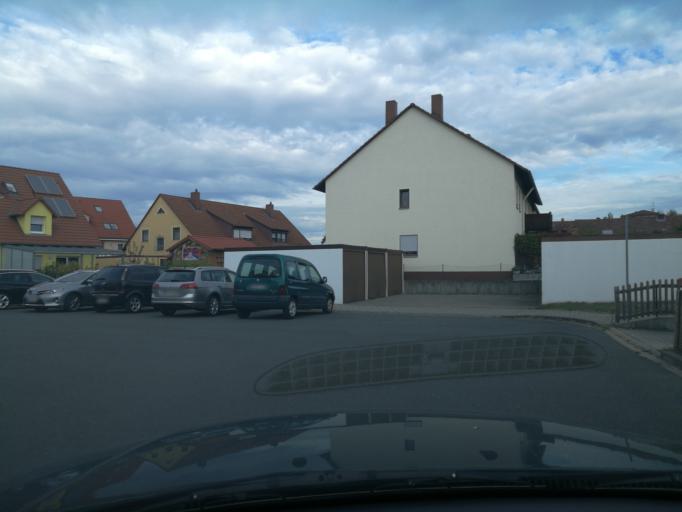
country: DE
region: Bavaria
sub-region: Regierungsbezirk Mittelfranken
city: Furth
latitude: 49.4863
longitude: 10.9694
